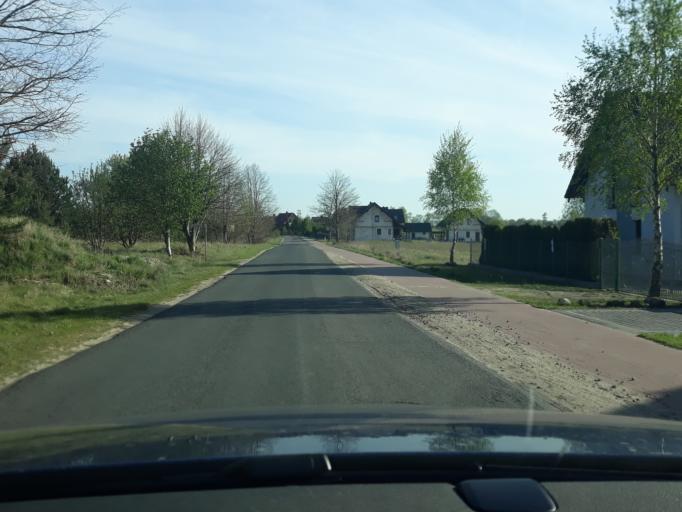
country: PL
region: Pomeranian Voivodeship
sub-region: Powiat czluchowski
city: Przechlewo
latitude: 53.8295
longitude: 17.3770
